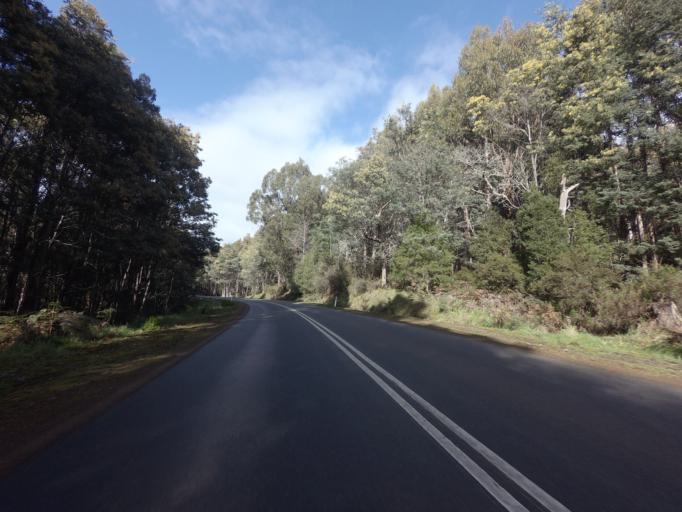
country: AU
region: Tasmania
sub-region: Huon Valley
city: Geeveston
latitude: -43.3443
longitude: 146.9618
